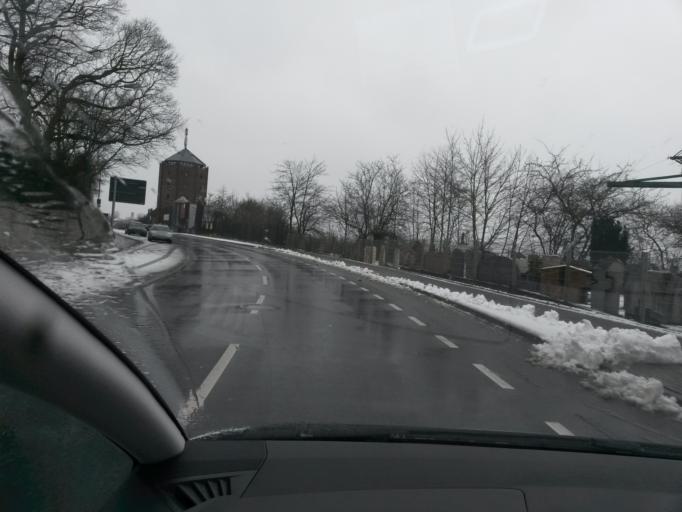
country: DE
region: Hesse
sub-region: Regierungsbezirk Kassel
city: Fulda
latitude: 50.5448
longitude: 9.6917
